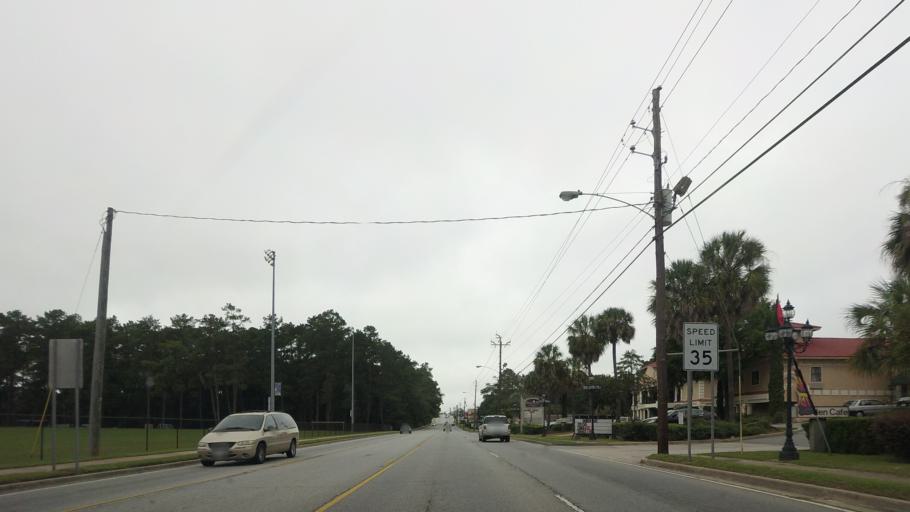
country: US
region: Georgia
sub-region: Lowndes County
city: Valdosta
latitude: 30.8652
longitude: -83.2852
